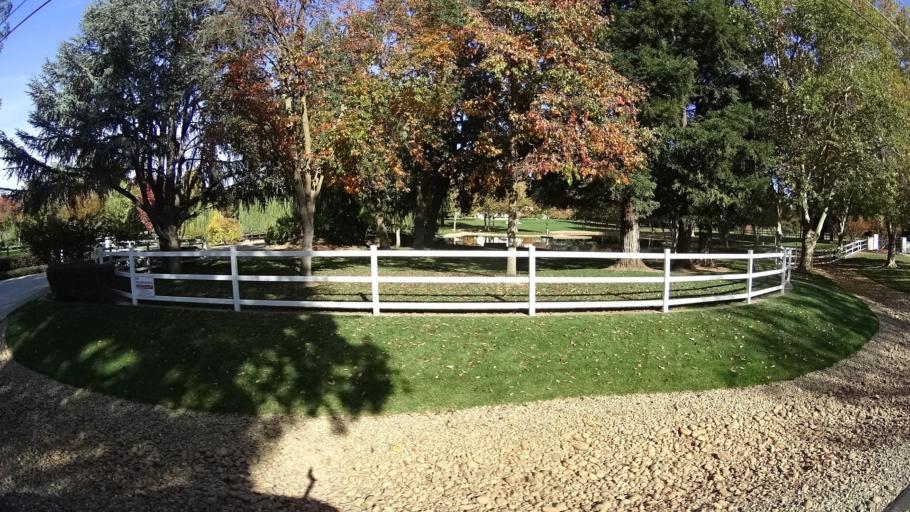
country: US
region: California
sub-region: Sacramento County
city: Wilton
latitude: 38.4319
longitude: -121.2916
